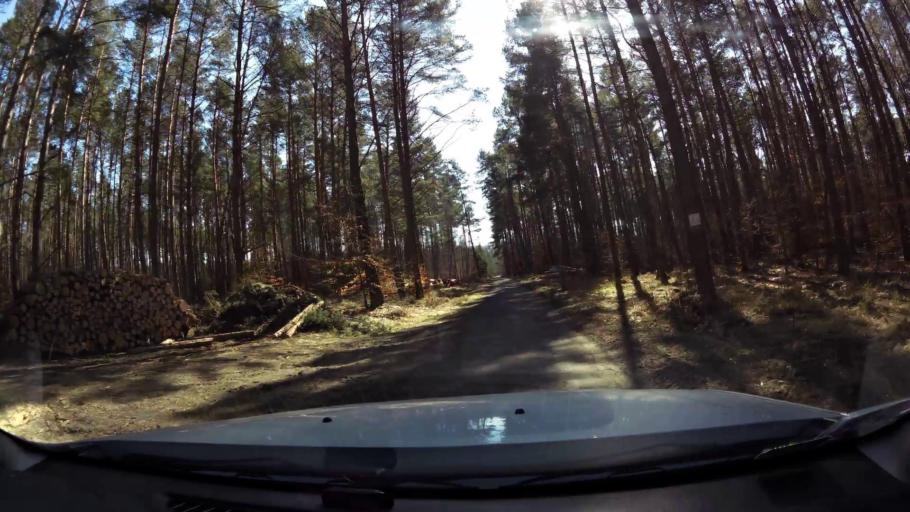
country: PL
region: West Pomeranian Voivodeship
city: Trzcinsko Zdroj
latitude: 53.0305
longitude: 14.6336
